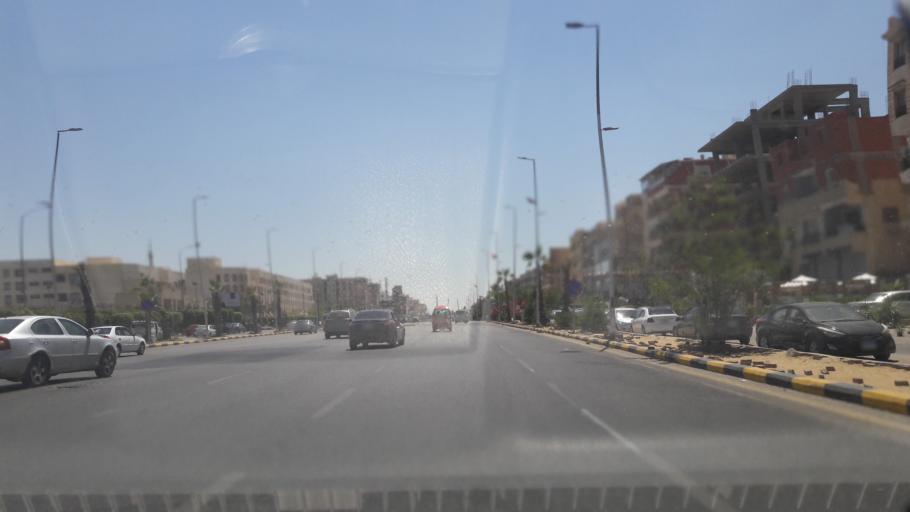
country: EG
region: Al Jizah
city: Madinat Sittah Uktubar
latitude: 29.9789
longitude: 30.9480
